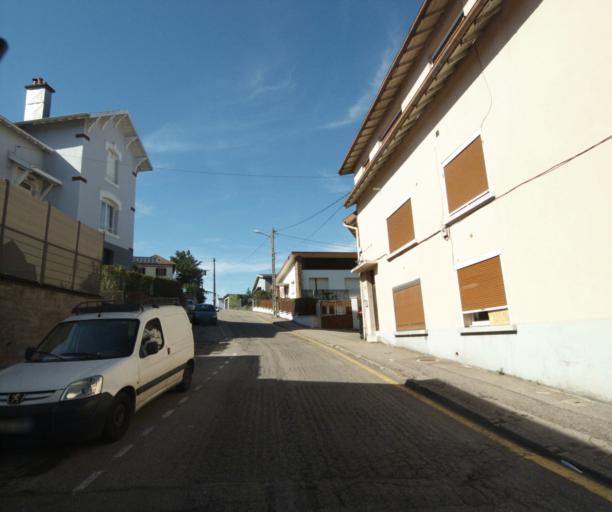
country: FR
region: Lorraine
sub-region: Departement des Vosges
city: Chantraine
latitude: 48.1774
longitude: 6.4398
